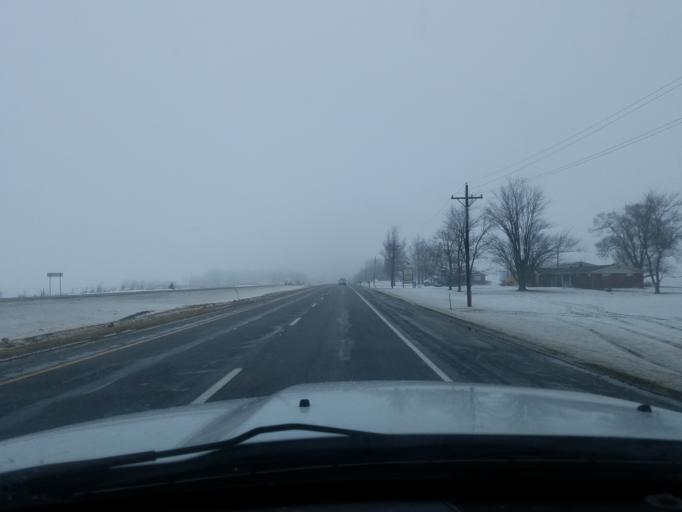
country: US
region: Indiana
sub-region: Howard County
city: Indian Heights
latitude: 40.3475
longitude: -86.1270
